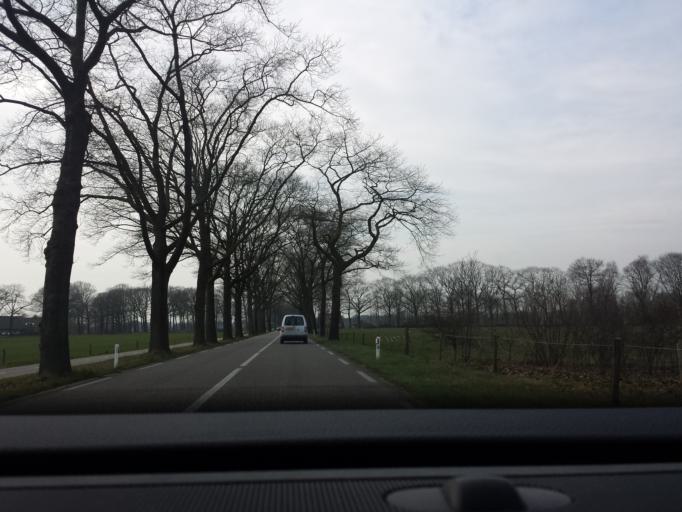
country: NL
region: Gelderland
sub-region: Gemeente Bronckhorst
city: Zelhem
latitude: 52.0027
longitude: 6.3891
